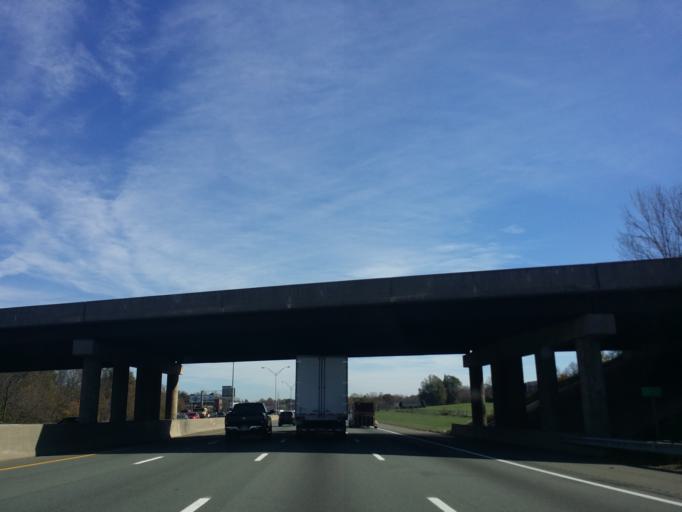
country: US
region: North Carolina
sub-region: Alamance County
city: Burlington
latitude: 36.0648
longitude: -79.4501
